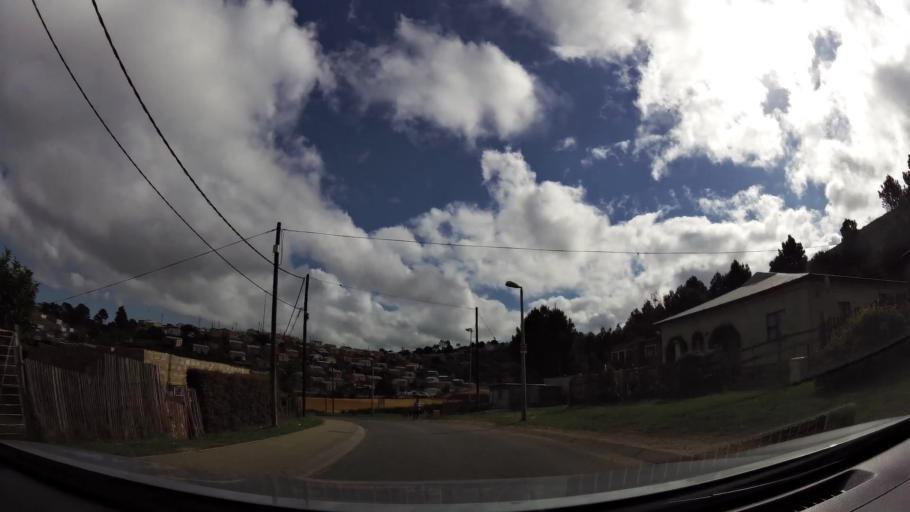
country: ZA
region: Western Cape
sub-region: Eden District Municipality
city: Knysna
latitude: -34.0331
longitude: 23.1041
